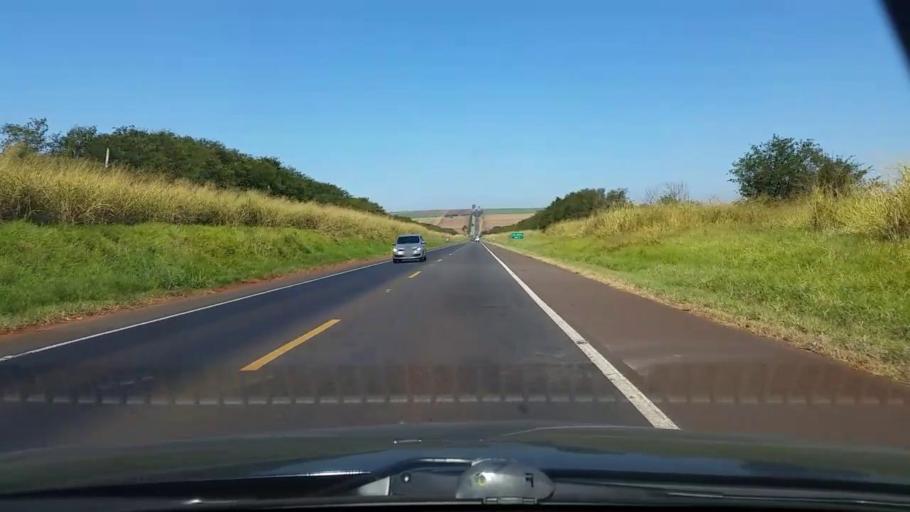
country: BR
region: Sao Paulo
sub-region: Jau
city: Jau
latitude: -22.3619
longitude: -48.5718
